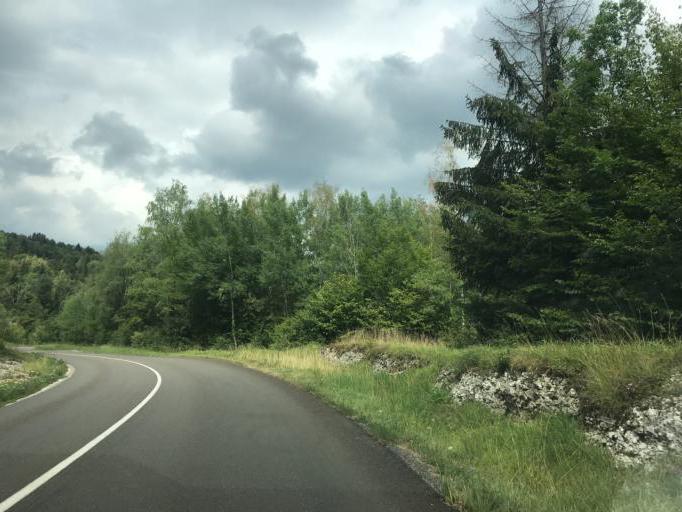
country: FR
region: Franche-Comte
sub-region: Departement du Jura
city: Valfin-les-Saint-Claude
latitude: 46.4422
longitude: 5.8564
